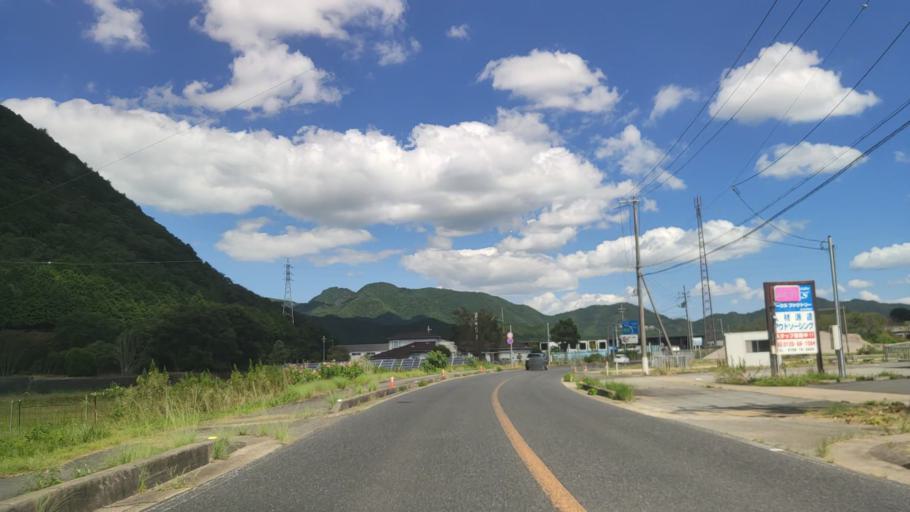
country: JP
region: Kyoto
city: Fukuchiyama
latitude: 35.1613
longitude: 135.0640
